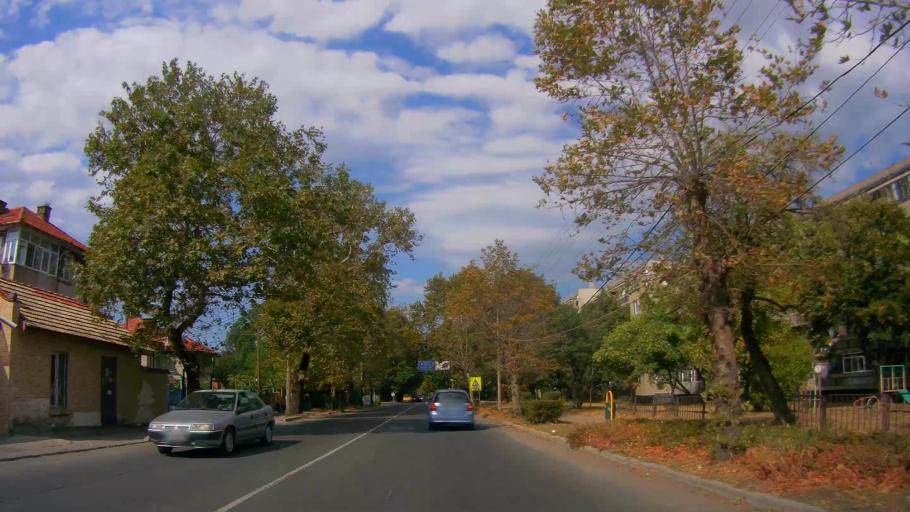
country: BG
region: Burgas
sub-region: Obshtina Aytos
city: Aytos
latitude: 42.6981
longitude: 27.2541
